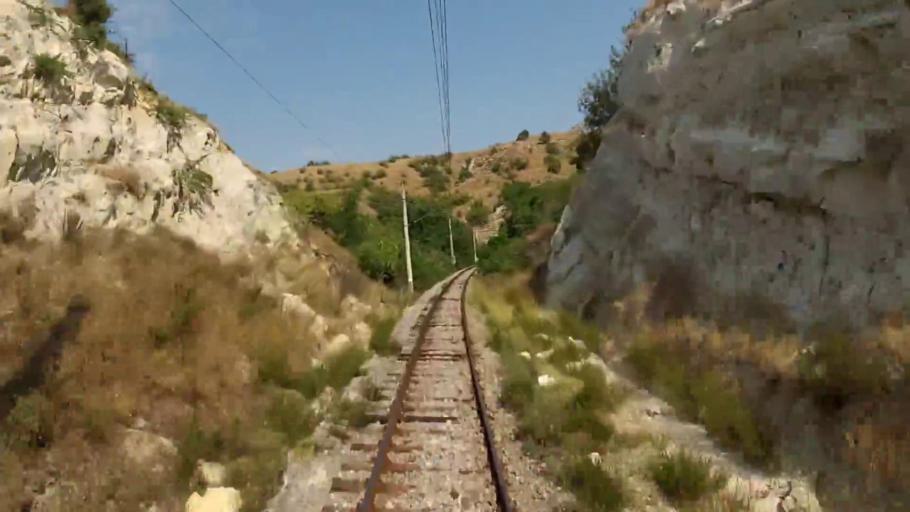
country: BG
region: Blagoevgrad
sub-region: Obshtina Petrich
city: Petrich
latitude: 41.4288
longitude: 23.3314
